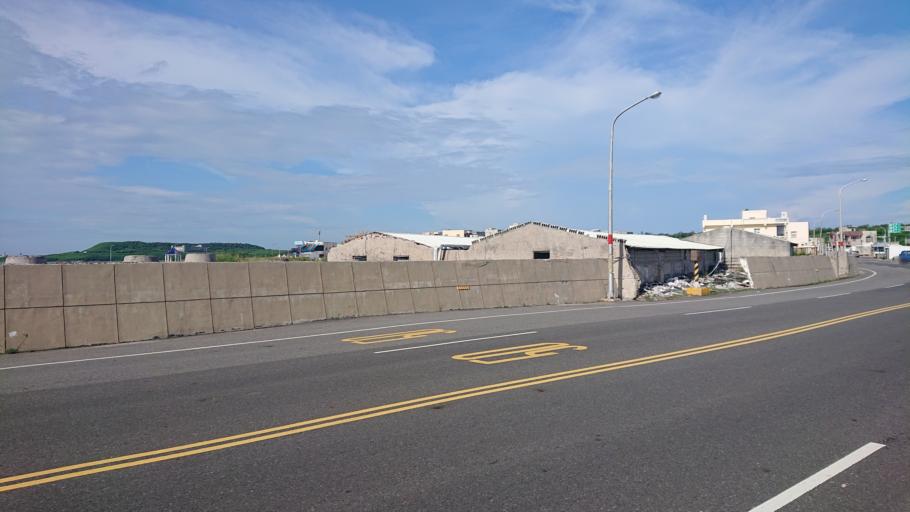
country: TW
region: Taiwan
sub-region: Penghu
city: Ma-kung
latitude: 23.5195
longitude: 119.5743
